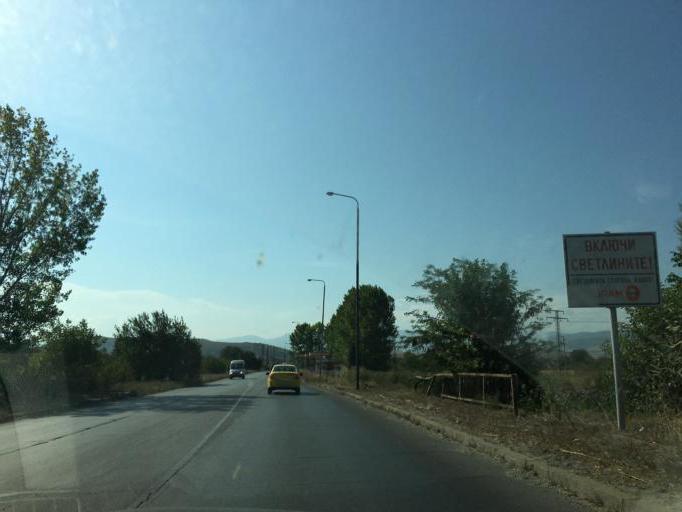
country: BG
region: Pazardzhik
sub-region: Obshtina Pazardzhik
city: Pazardzhik
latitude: 42.1675
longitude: 24.3150
